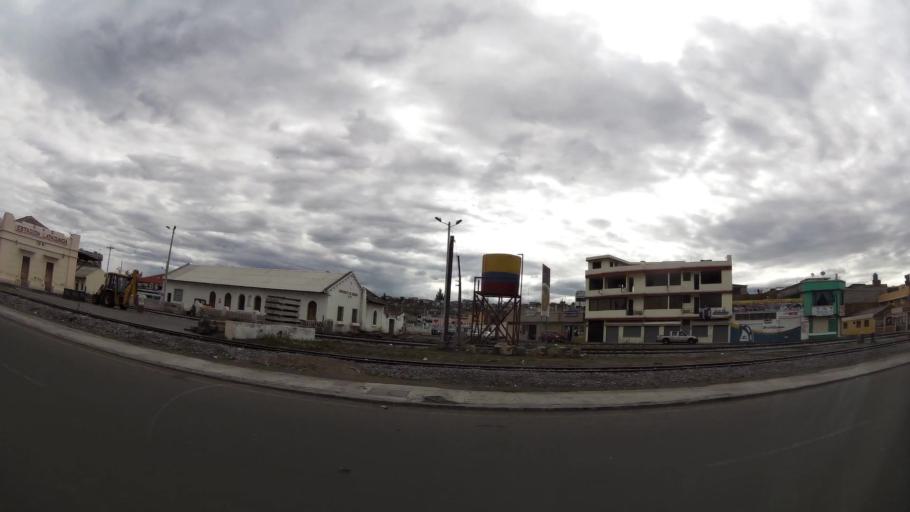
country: EC
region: Cotopaxi
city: Latacunga
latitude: -0.9316
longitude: -78.6231
